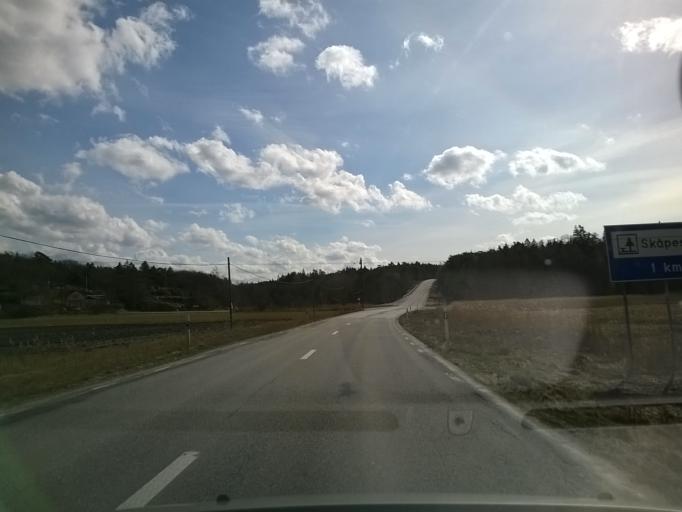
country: SE
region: Vaestra Goetaland
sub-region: Tjorns Kommun
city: Myggenas
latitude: 58.1021
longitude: 11.7071
